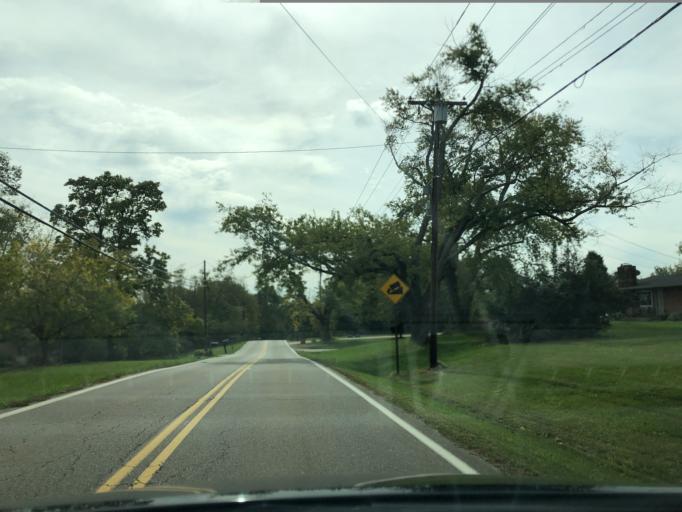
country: US
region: Ohio
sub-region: Hamilton County
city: The Village of Indian Hill
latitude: 39.2214
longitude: -84.3018
